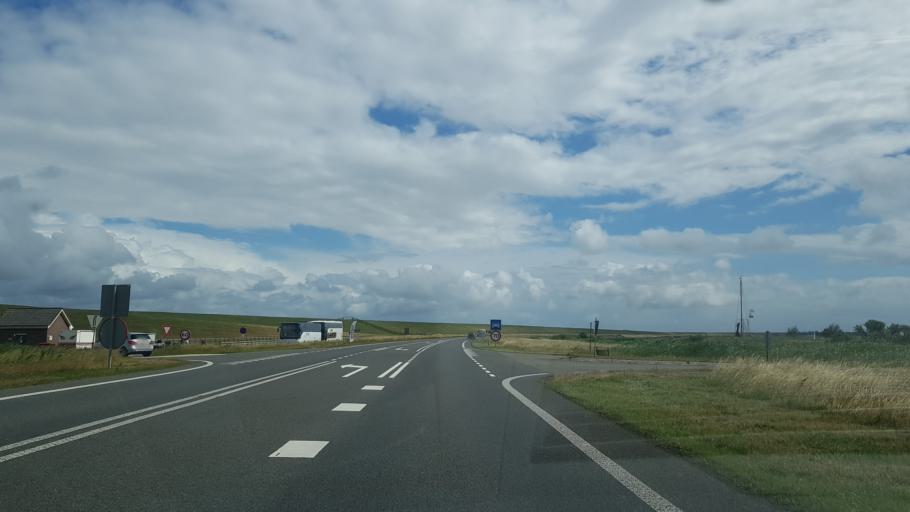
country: NL
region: Friesland
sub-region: Gemeente Dongeradeel
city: Anjum
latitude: 53.4070
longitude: 6.1563
